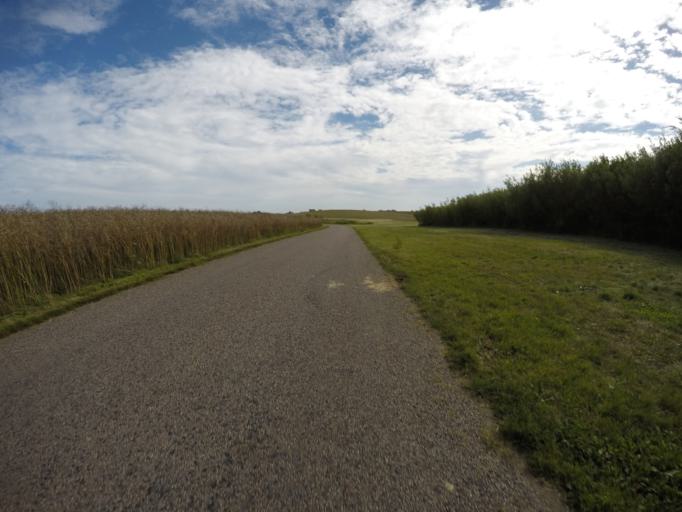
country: SE
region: Skane
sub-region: Simrishamns Kommun
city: Simrishamn
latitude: 55.4986
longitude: 14.2312
